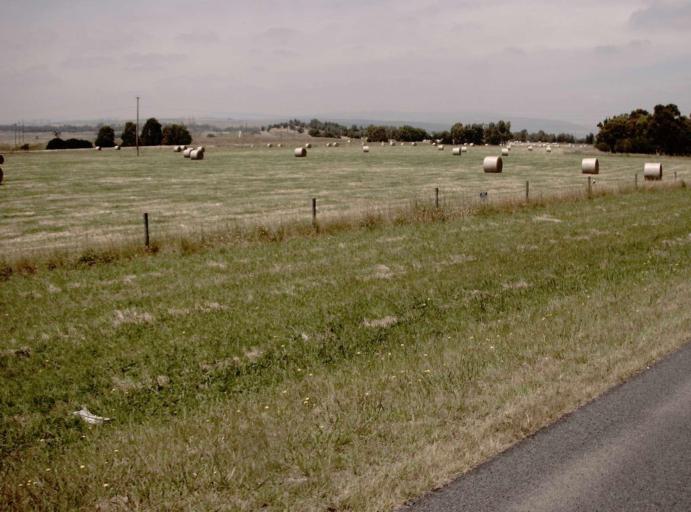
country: AU
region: Victoria
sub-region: Latrobe
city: Traralgon
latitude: -38.2281
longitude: 146.5415
